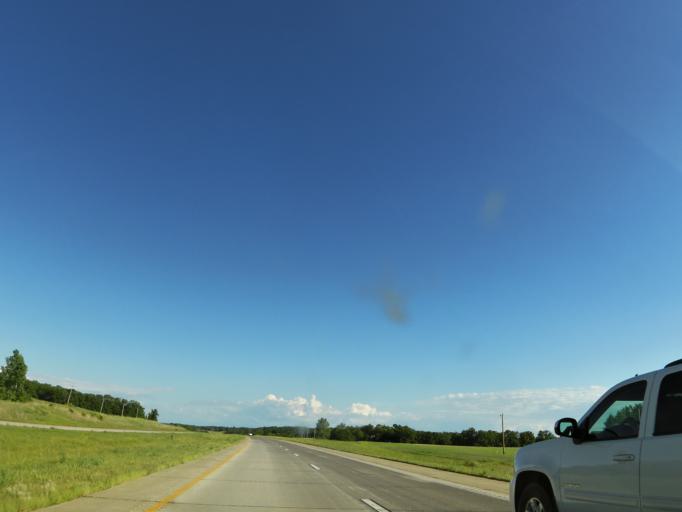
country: US
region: Missouri
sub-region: Pike County
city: Bowling Green
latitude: 39.4182
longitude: -91.2517
